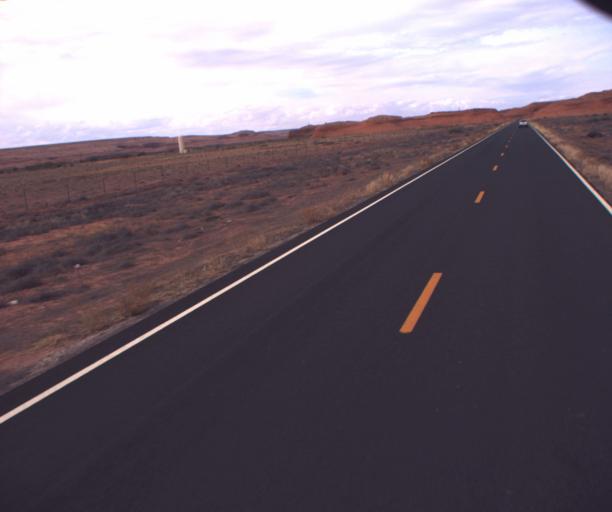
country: US
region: Arizona
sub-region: Apache County
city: Many Farms
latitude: 36.7578
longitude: -109.6481
